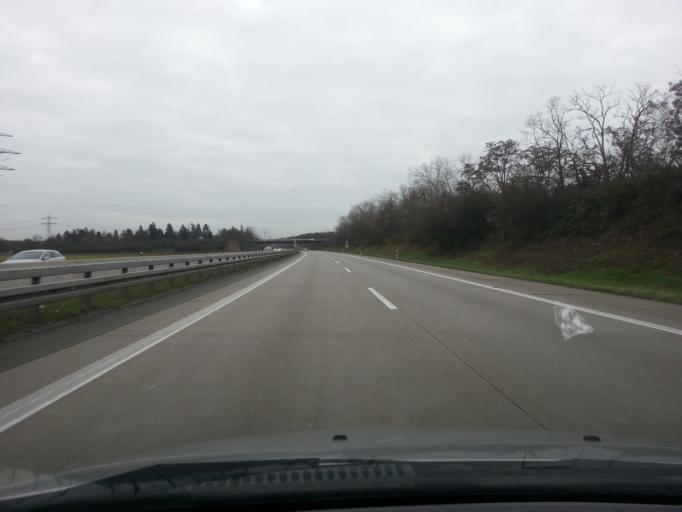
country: DE
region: Baden-Wuerttemberg
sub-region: Karlsruhe Region
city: Bruhl
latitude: 49.4395
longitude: 8.5402
